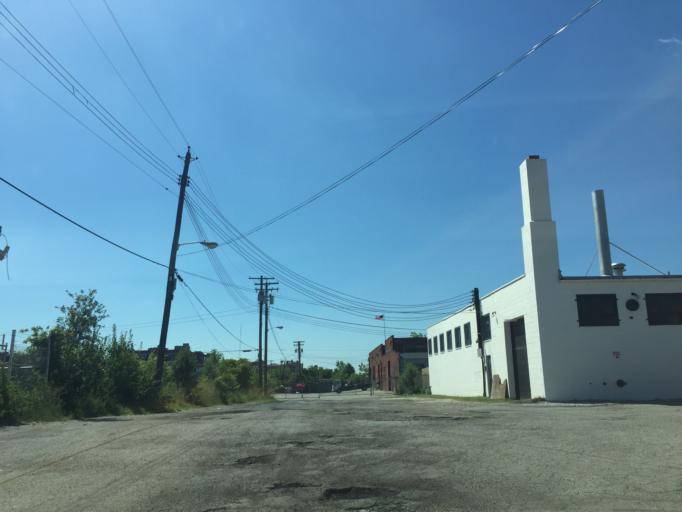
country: US
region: Maryland
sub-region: City of Baltimore
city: Baltimore
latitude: 39.2907
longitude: -76.5608
